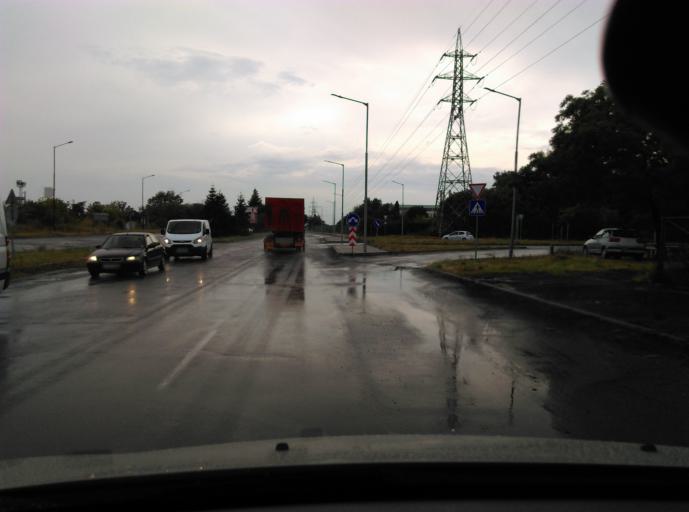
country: BG
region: Burgas
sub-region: Obshtina Burgas
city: Burgas
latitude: 42.5157
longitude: 27.4361
